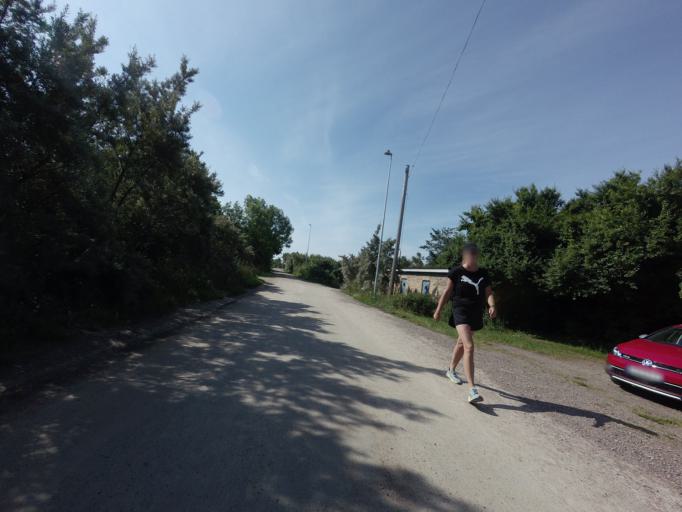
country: SE
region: Skane
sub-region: Helsingborg
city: Rydeback
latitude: 55.9648
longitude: 12.7585
